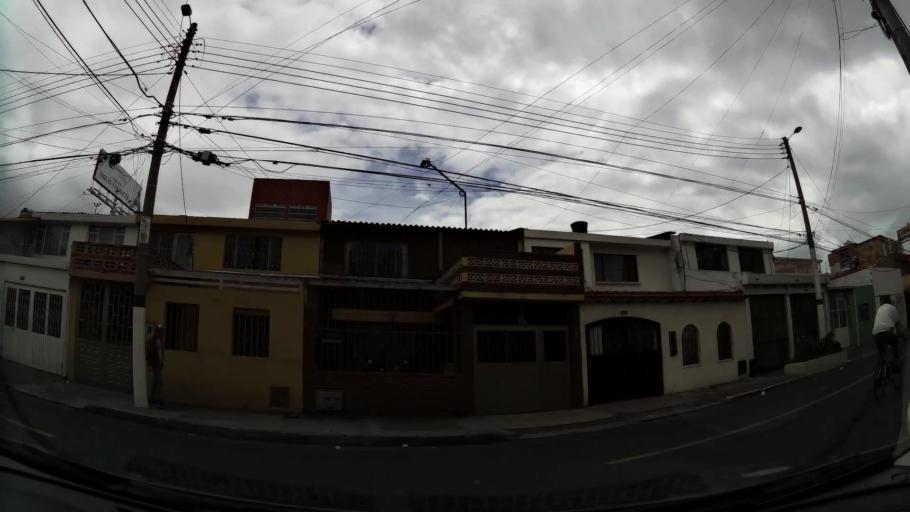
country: CO
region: Bogota D.C.
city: Barrio San Luis
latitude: 4.6941
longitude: -74.0884
